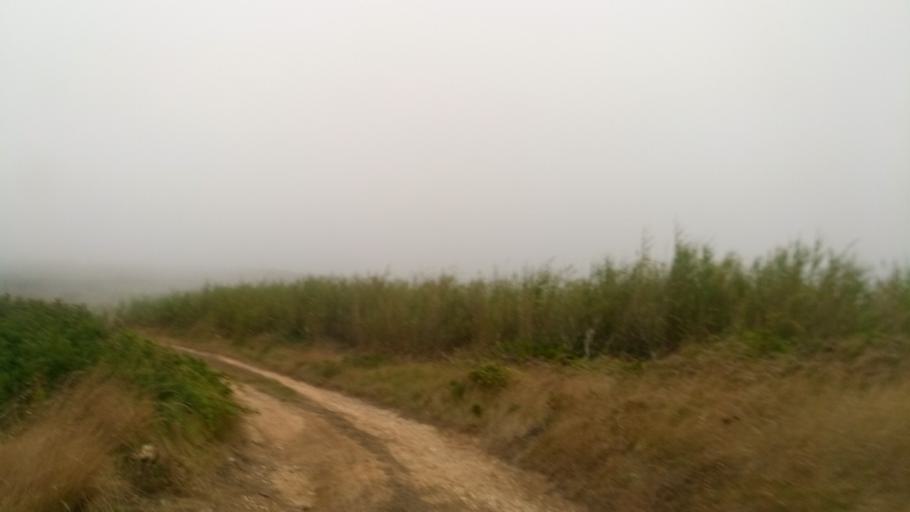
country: PT
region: Leiria
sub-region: Caldas da Rainha
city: Caldas da Rainha
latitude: 39.4672
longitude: -9.2001
